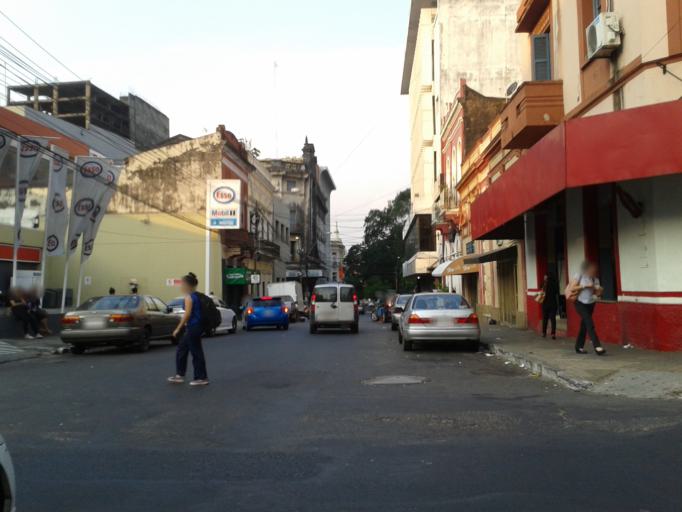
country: PY
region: Asuncion
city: Asuncion
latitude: -25.2841
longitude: -57.6364
